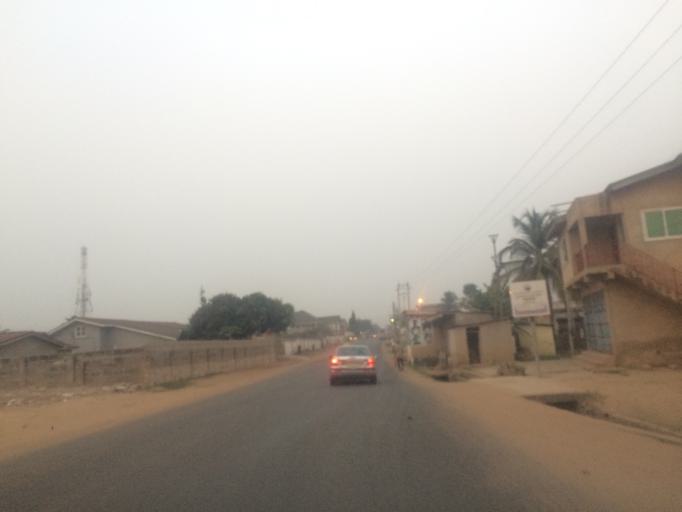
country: GH
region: Greater Accra
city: Nungua
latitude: 5.6007
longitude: -0.0942
